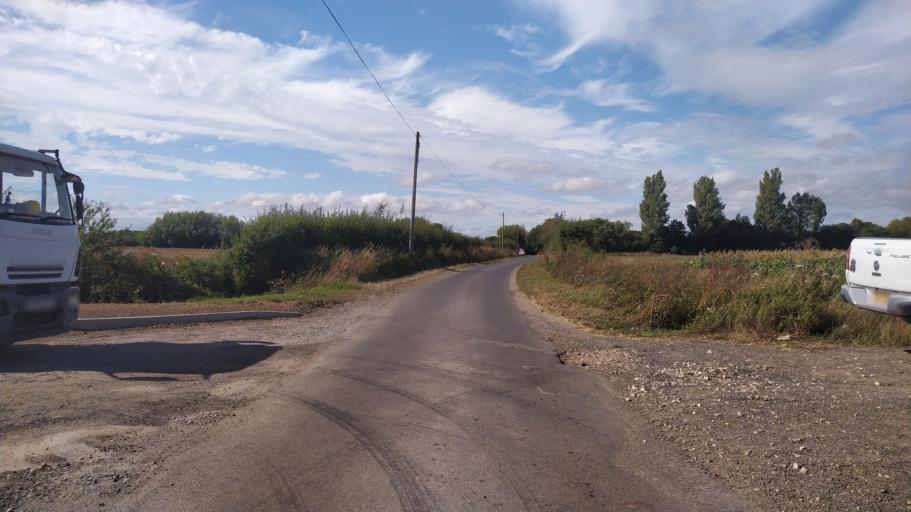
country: GB
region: England
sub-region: West Sussex
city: Chichester
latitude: 50.8039
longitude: -0.7606
